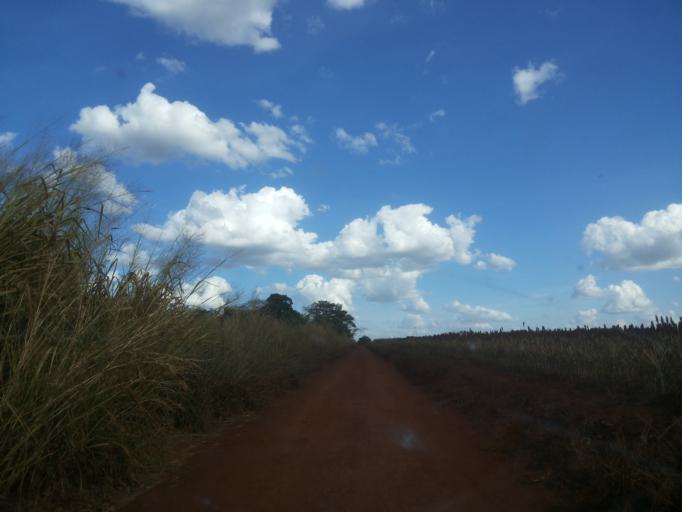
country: BR
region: Minas Gerais
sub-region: Capinopolis
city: Capinopolis
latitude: -18.5994
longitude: -49.4952
